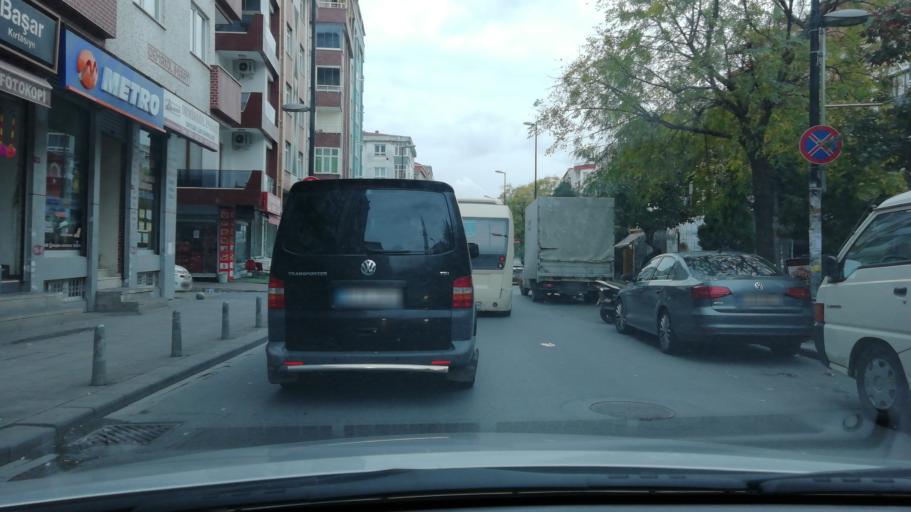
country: TR
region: Istanbul
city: Bahcelievler
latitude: 41.0027
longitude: 28.8388
